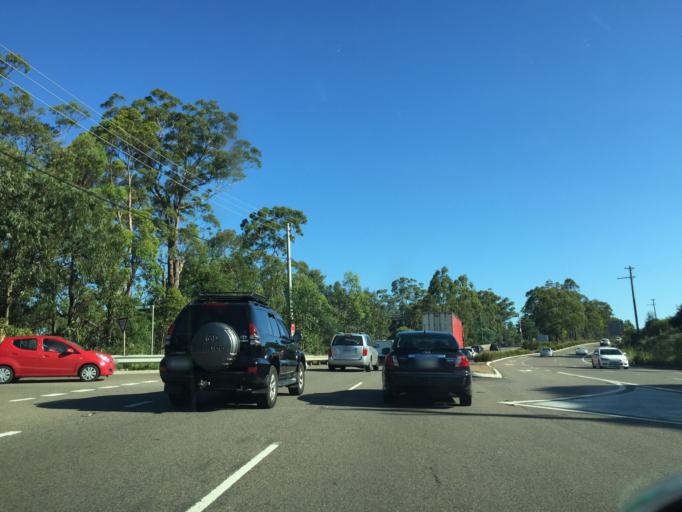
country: AU
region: New South Wales
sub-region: Blue Mountains Municipality
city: Blaxland
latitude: -33.7141
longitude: 150.5940
